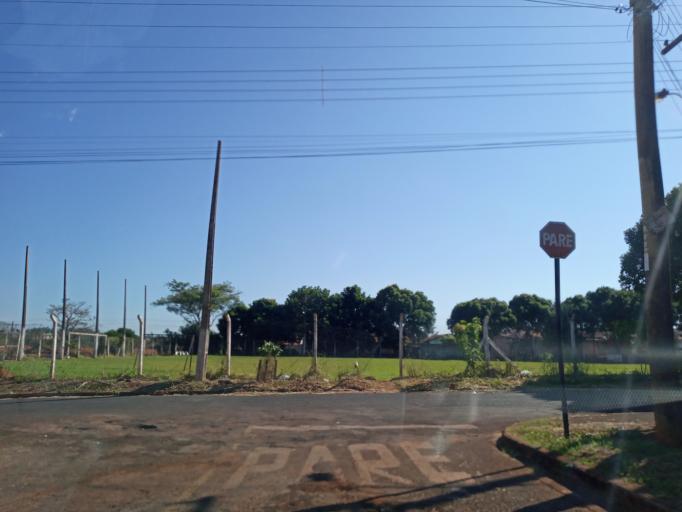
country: BR
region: Minas Gerais
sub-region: Ituiutaba
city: Ituiutaba
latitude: -18.9792
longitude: -49.4903
